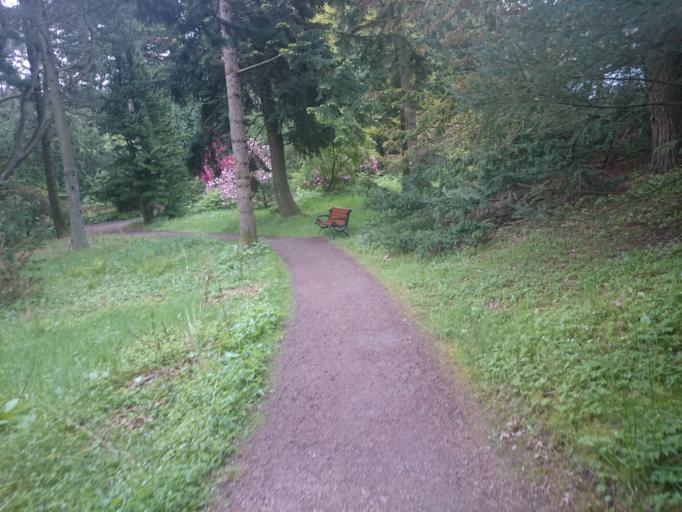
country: SE
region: Vaestra Goetaland
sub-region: Goteborg
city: Goeteborg
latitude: 57.6810
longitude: 11.9527
